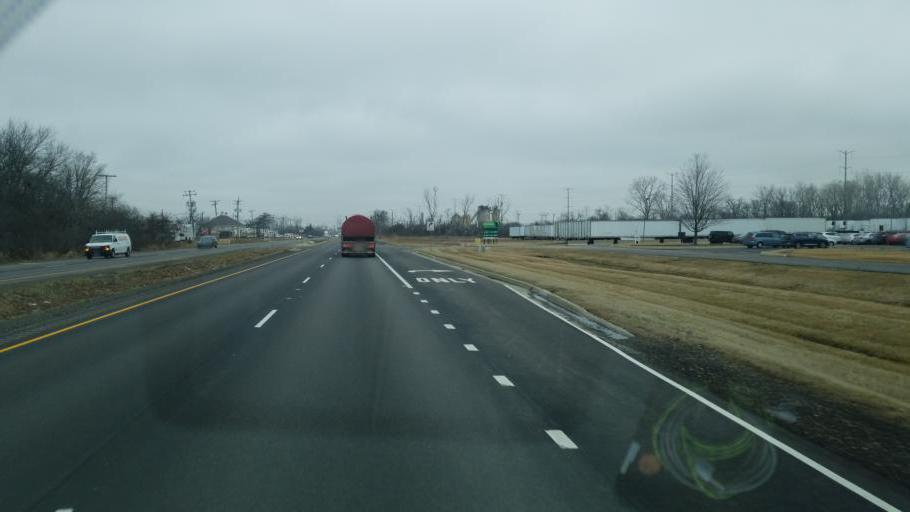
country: US
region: Illinois
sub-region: Lake County
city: Knollwood
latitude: 42.2930
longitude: -87.8757
